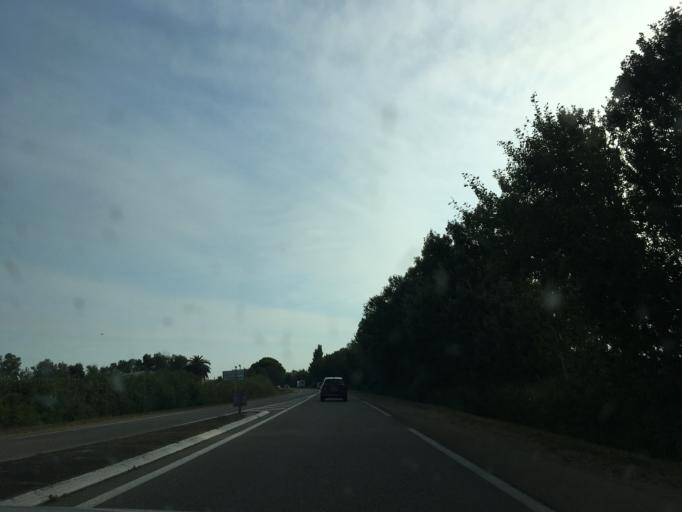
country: FR
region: Languedoc-Roussillon
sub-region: Departement du Gard
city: Saint-Gilles
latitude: 43.5922
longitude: 4.4676
